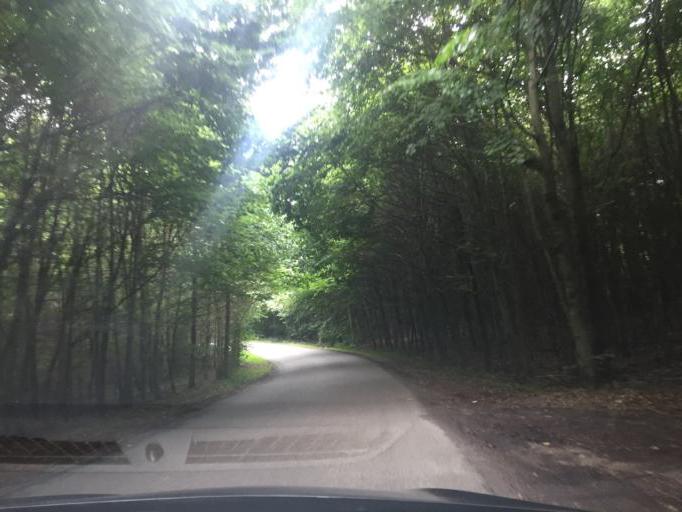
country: DK
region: South Denmark
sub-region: Assens Kommune
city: Tommerup Stationsby
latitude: 55.3725
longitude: 10.2207
